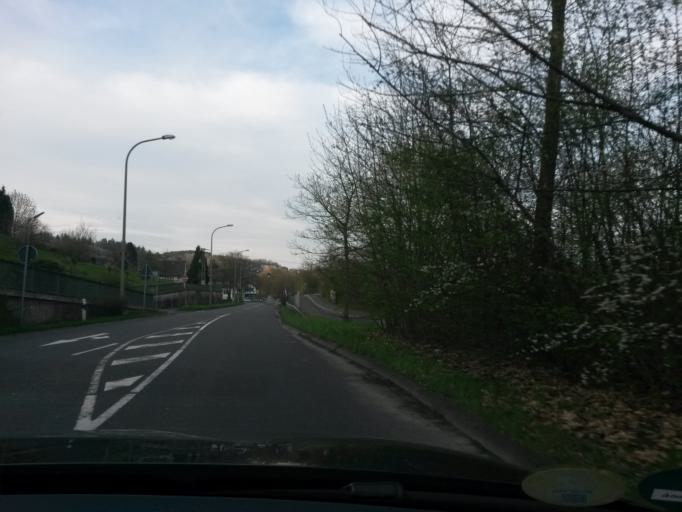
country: DE
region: North Rhine-Westphalia
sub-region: Regierungsbezirk Koln
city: Overath
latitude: 50.9247
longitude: 7.2724
